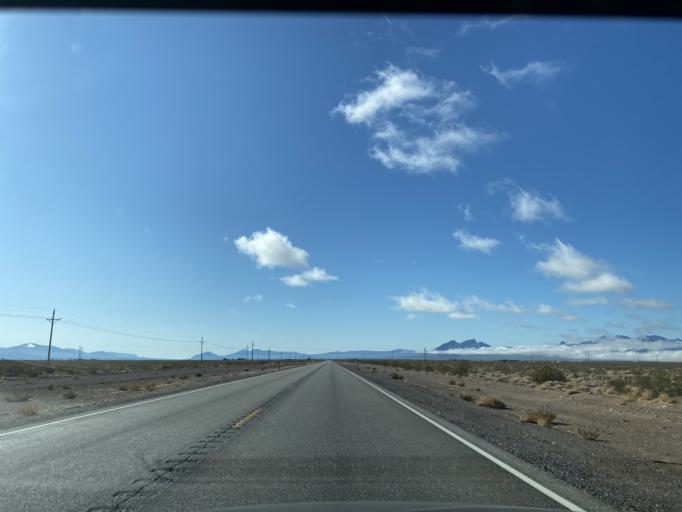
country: US
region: Nevada
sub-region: Nye County
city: Beatty
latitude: 36.5449
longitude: -116.4173
